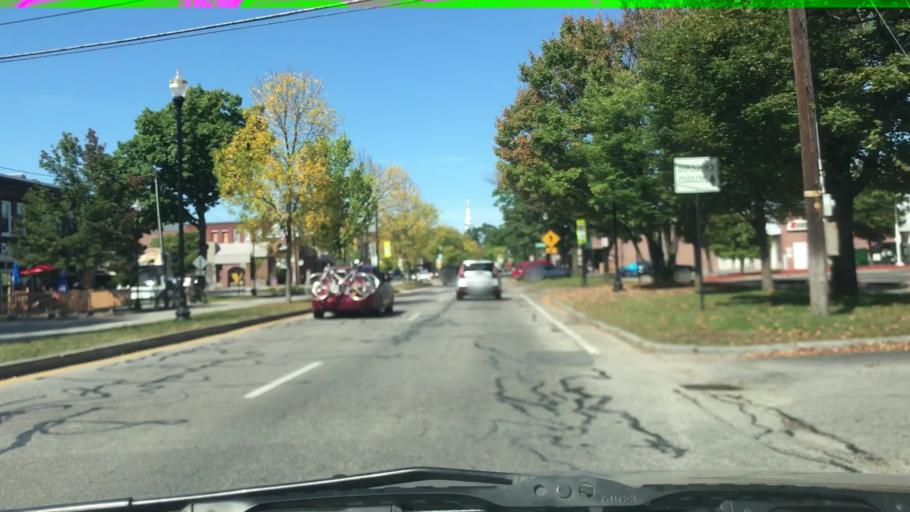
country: US
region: New Hampshire
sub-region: Cheshire County
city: Keene
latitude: 42.9299
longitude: -72.2777
